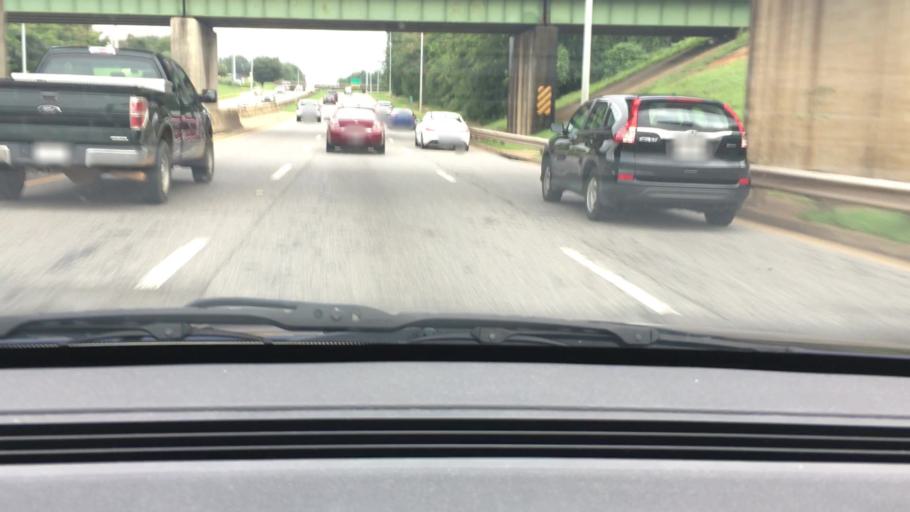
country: US
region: Alabama
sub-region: Tuscaloosa County
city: Tuscaloosa
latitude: 33.2019
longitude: -87.5251
